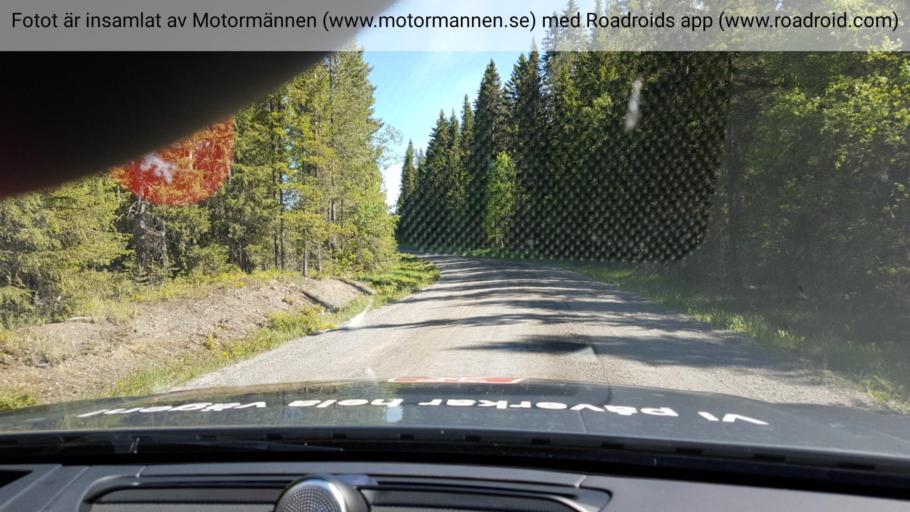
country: SE
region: Jaemtland
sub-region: OEstersunds Kommun
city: Brunflo
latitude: 63.0170
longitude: 14.7714
